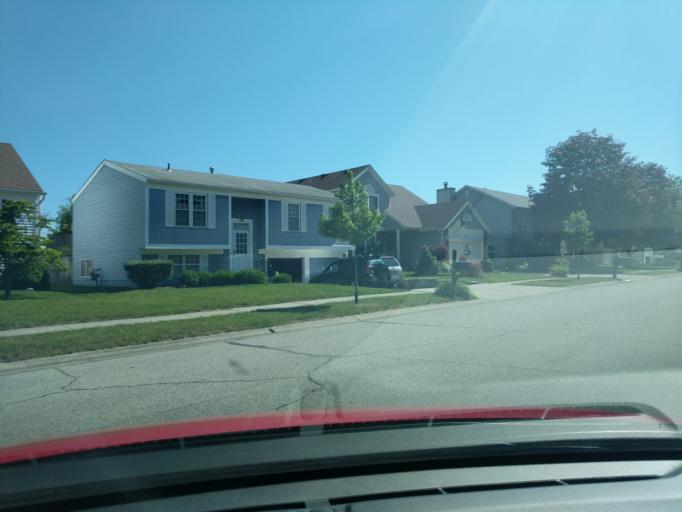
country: US
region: Ohio
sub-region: Franklin County
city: Huber Ridge
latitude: 40.0657
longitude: -82.9105
